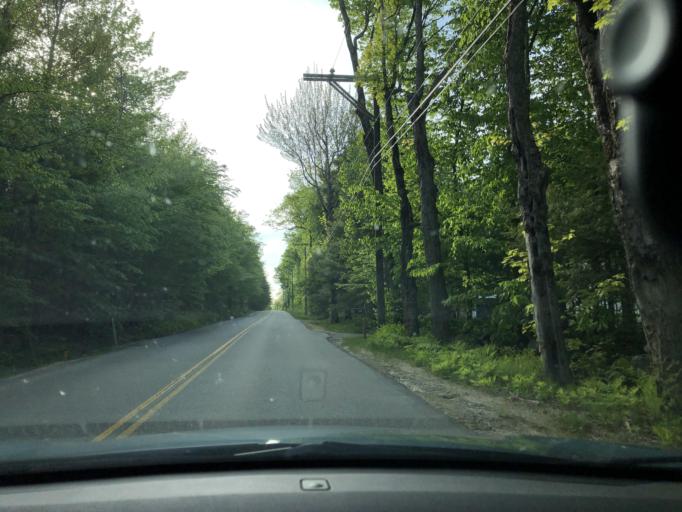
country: US
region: New Hampshire
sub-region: Merrimack County
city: New London
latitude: 43.4119
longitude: -71.9672
